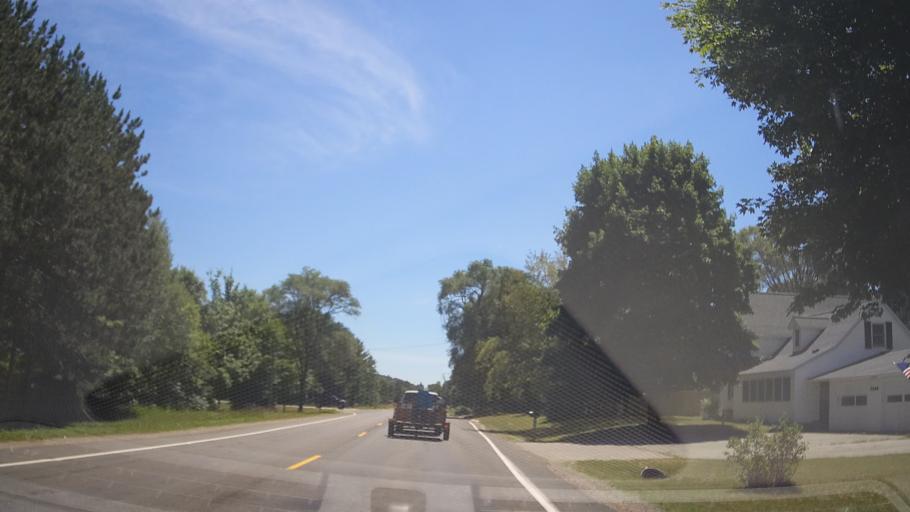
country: US
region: Michigan
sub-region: Grand Traverse County
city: Traverse City
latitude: 44.6444
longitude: -85.6964
